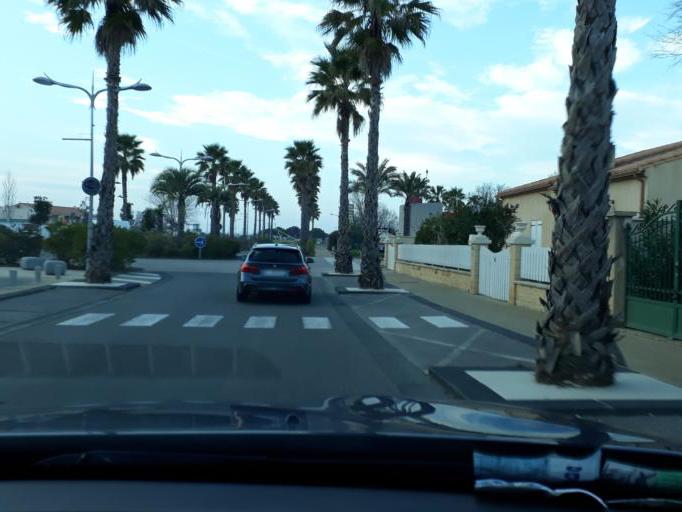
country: FR
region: Languedoc-Roussillon
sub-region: Departement de l'Herault
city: Marseillan
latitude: 43.3178
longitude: 3.5477
